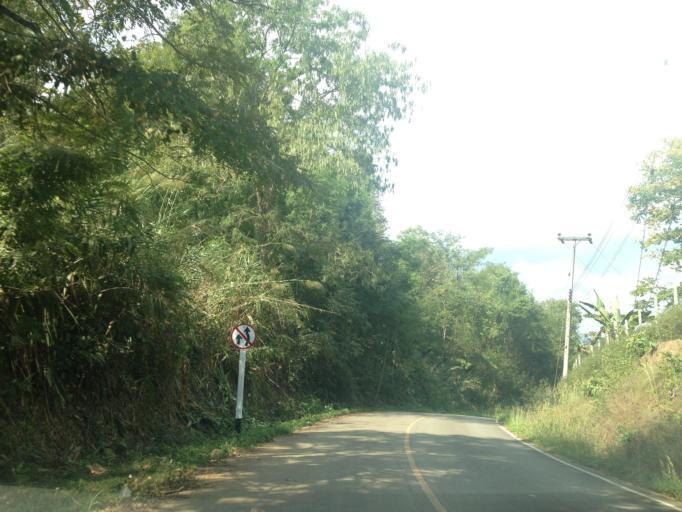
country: TH
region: Chiang Mai
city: Hang Dong
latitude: 18.7165
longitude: 98.8881
